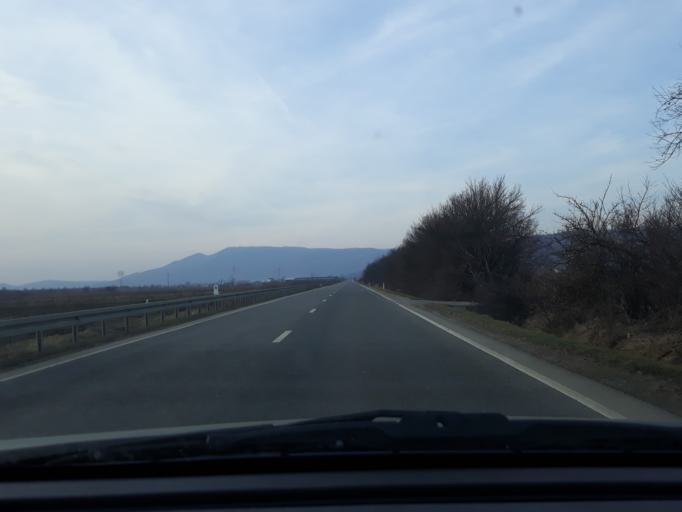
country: RO
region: Salaj
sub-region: Comuna Periceiu
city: Periceiu
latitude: 47.2172
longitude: 22.8929
